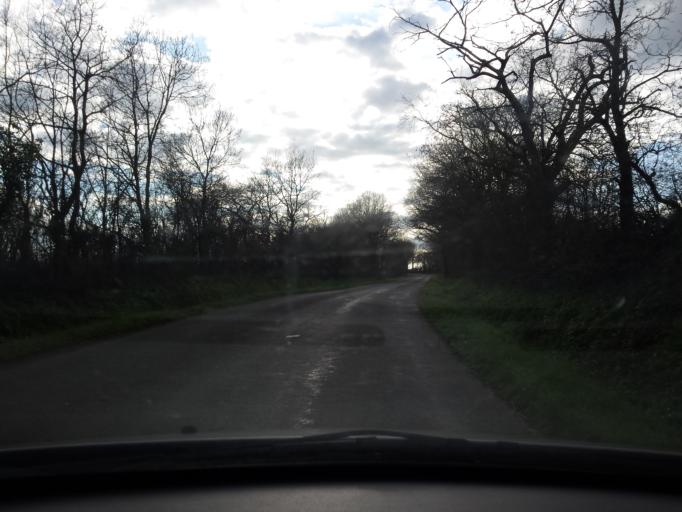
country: FR
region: Pays de la Loire
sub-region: Departement de la Vendee
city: Sainte-Cecile
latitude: 46.7224
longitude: -1.1330
